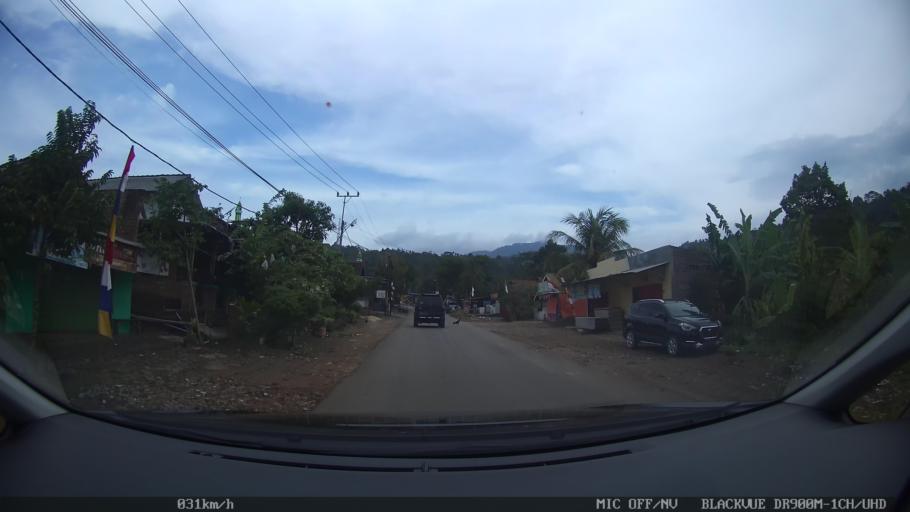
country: ID
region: Lampung
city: Kedaton
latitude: -5.3933
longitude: 105.1915
